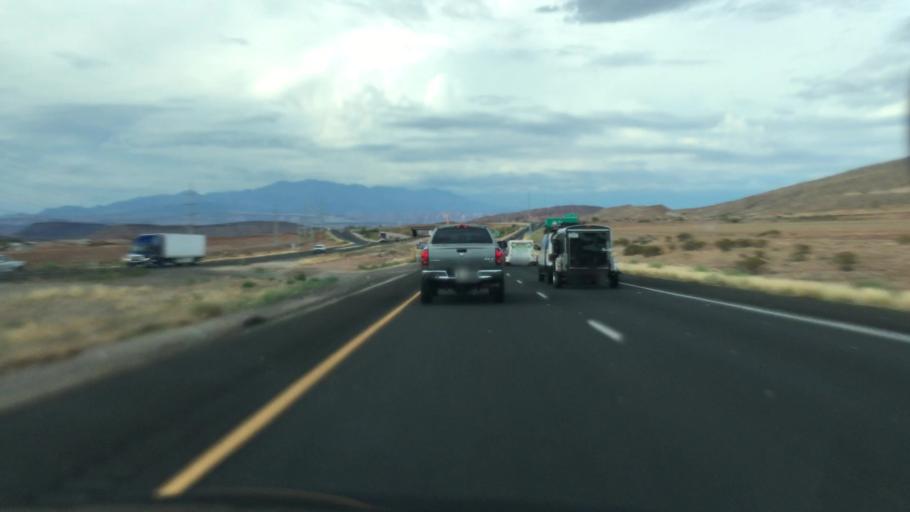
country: US
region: Utah
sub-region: Washington County
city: Saint George
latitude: 37.0220
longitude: -113.6085
